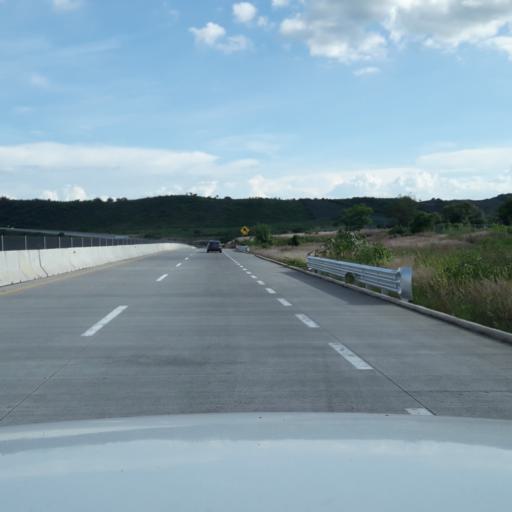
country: MX
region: Jalisco
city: Arenal
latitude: 20.7823
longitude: -103.7138
